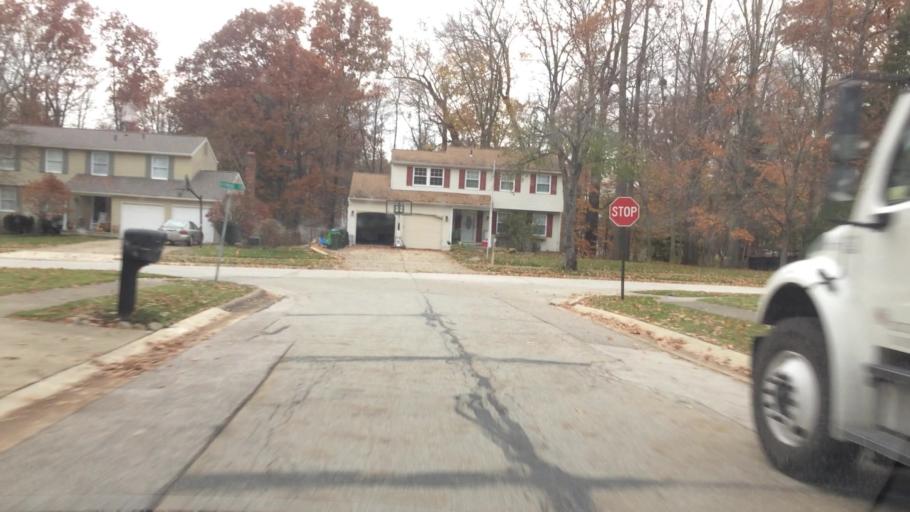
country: US
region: Ohio
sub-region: Summit County
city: Silver Lake
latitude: 41.1783
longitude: -81.4534
